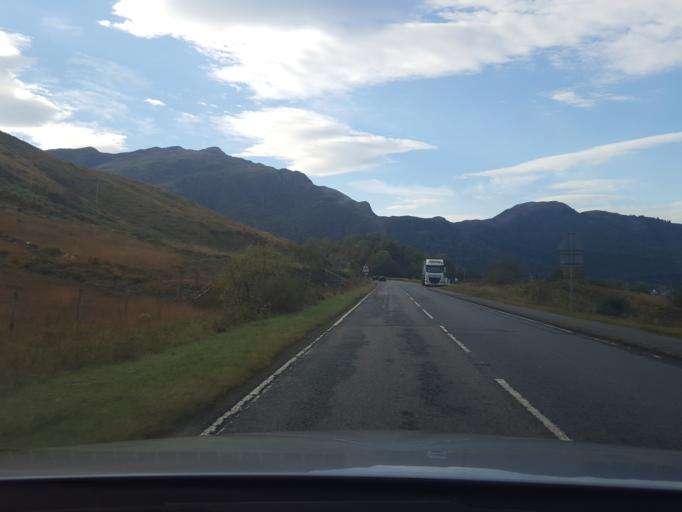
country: GB
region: Scotland
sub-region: Highland
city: Fort William
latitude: 57.2248
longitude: -5.4095
